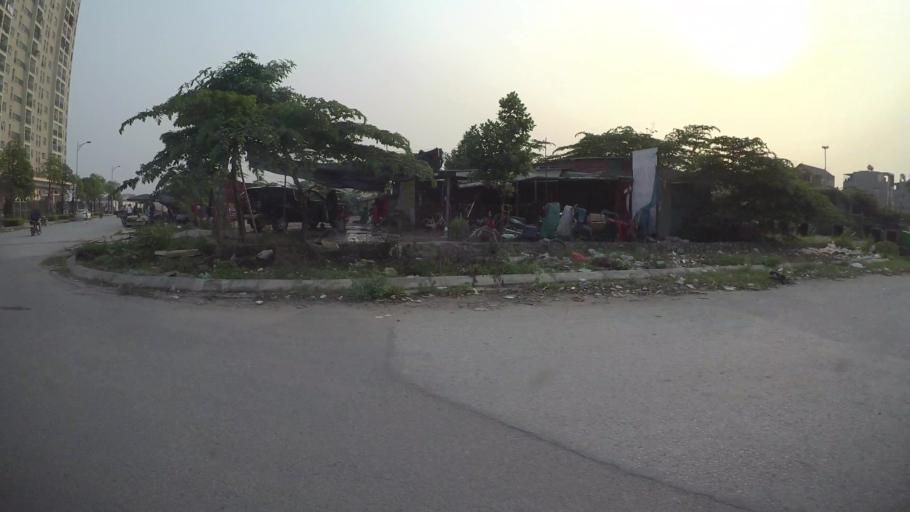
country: VN
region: Ha Noi
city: Cau Dien
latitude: 21.0070
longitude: 105.7265
